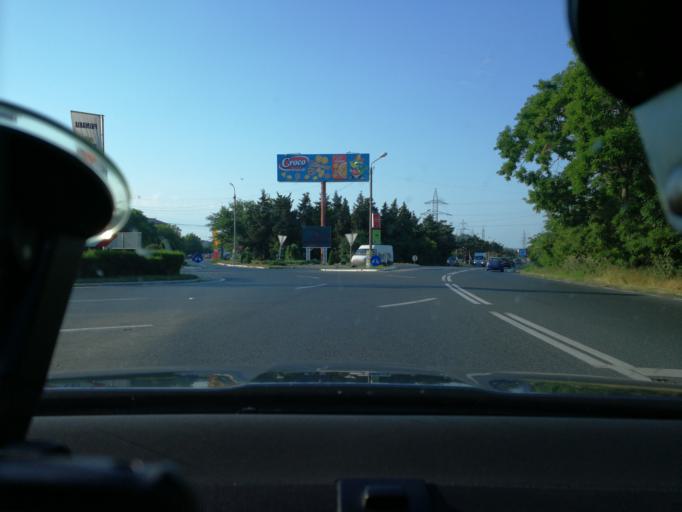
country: RO
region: Constanta
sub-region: Oras Eforie
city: Eforie Nord
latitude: 44.0739
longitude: 28.6272
